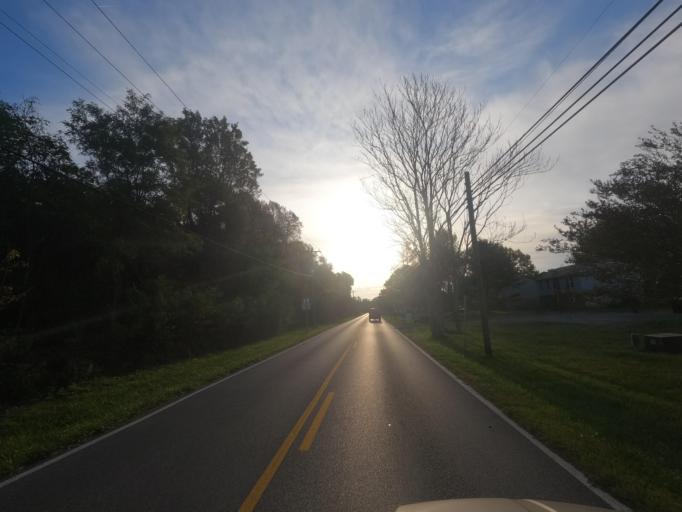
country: US
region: Maryland
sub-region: Calvert County
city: Lusby
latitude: 38.3878
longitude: -76.4294
